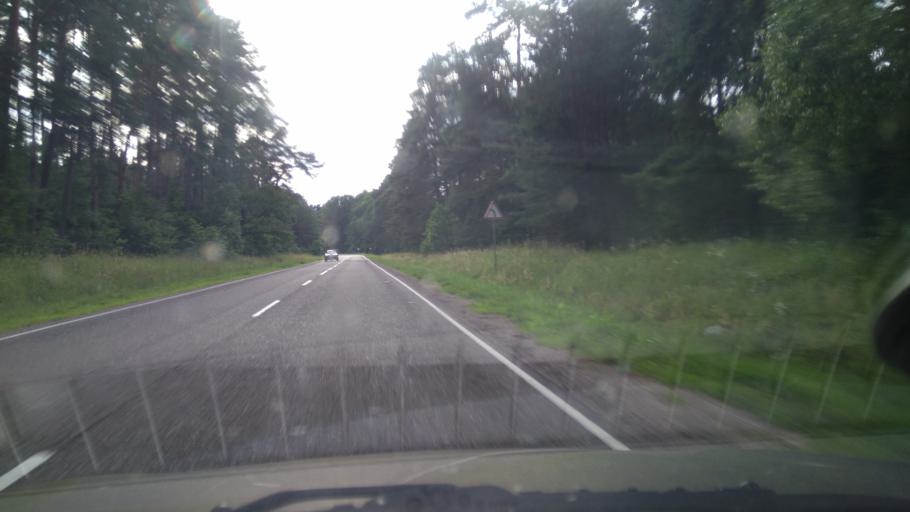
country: BY
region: Grodnenskaya
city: Masty
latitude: 53.3477
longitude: 24.6556
